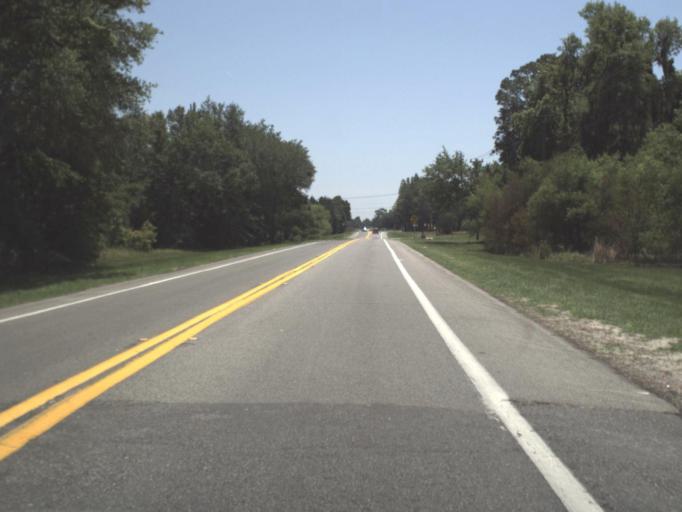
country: US
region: Florida
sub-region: Suwannee County
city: Live Oak
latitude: 30.3109
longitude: -83.0178
